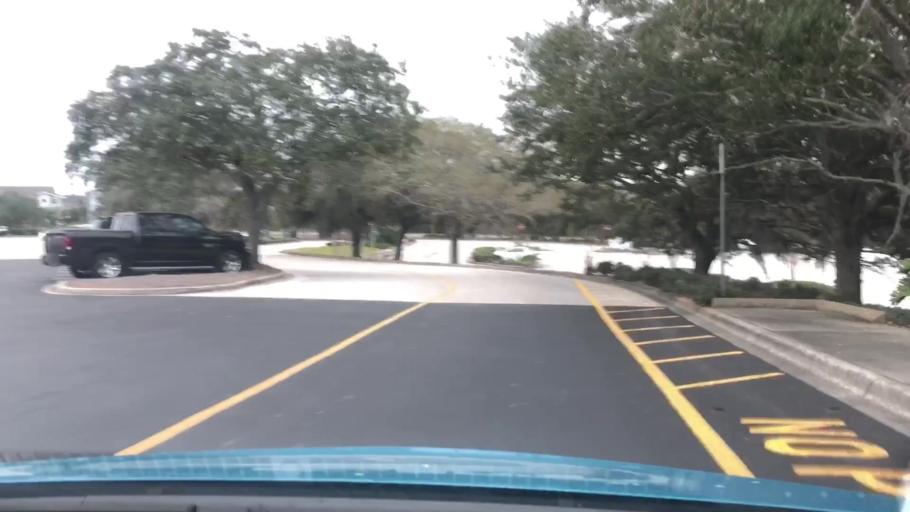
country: US
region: Florida
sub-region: Seminole County
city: Lake Mary
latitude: 28.8038
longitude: -81.3372
